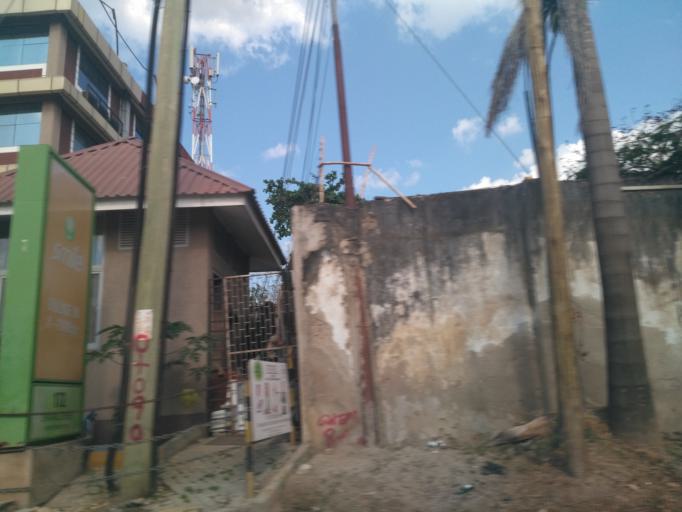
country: TZ
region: Dar es Salaam
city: Magomeni
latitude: -6.7706
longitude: 39.2608
